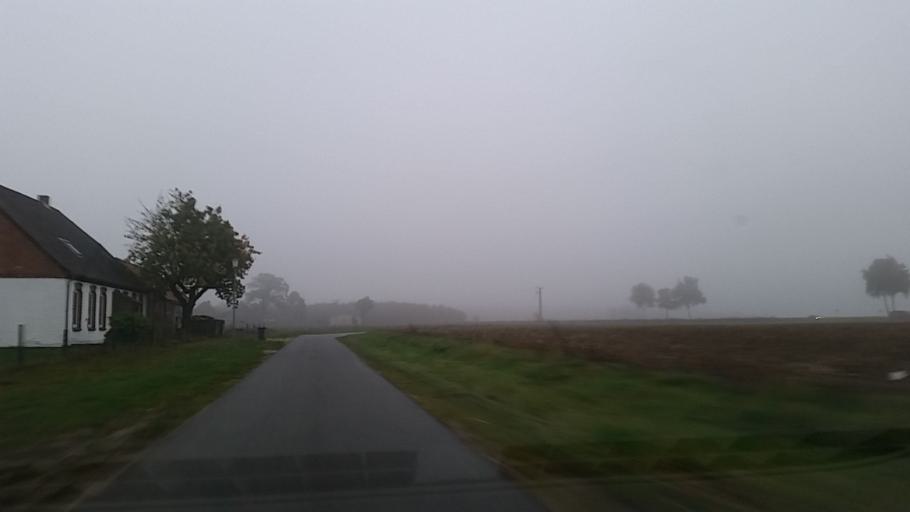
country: DE
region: Lower Saxony
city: Luder
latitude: 52.8066
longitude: 10.6725
